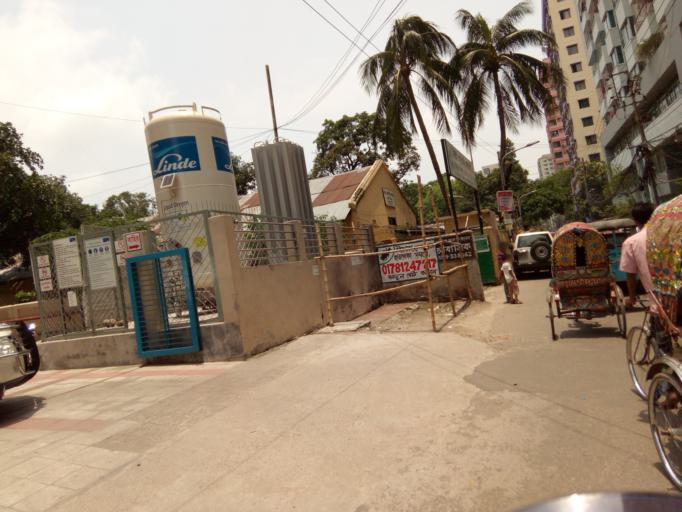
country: BD
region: Dhaka
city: Paltan
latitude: 23.7318
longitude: 90.4063
